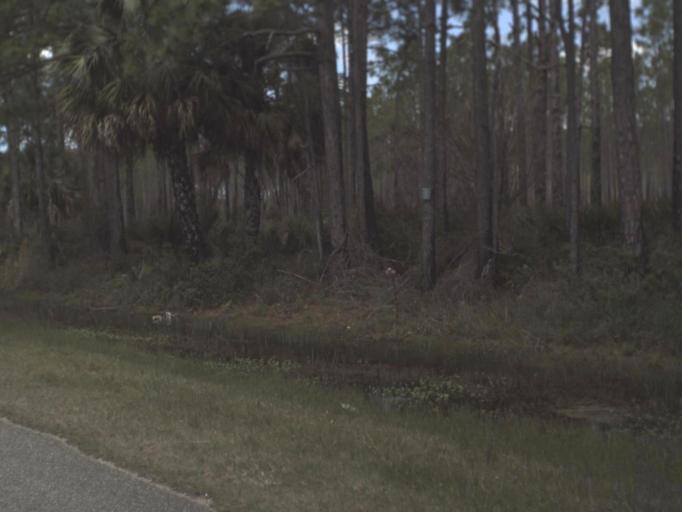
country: US
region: Florida
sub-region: Franklin County
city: Apalachicola
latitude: 29.7207
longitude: -85.1066
